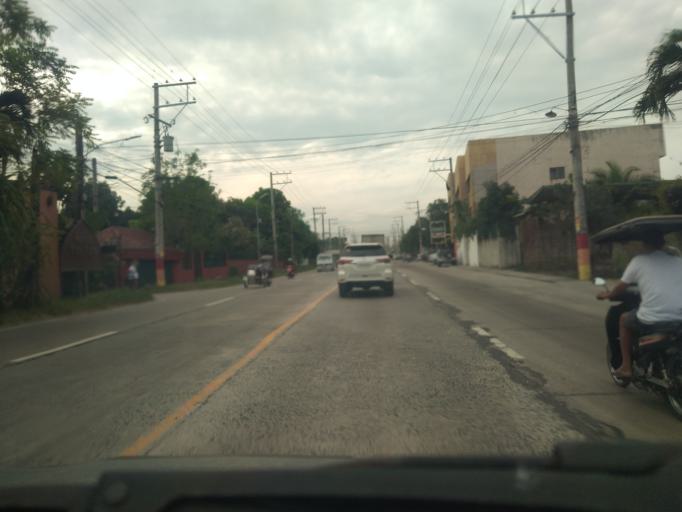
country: PH
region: Central Luzon
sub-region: Province of Pampanga
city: Del Pilar
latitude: 15.0310
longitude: 120.6966
